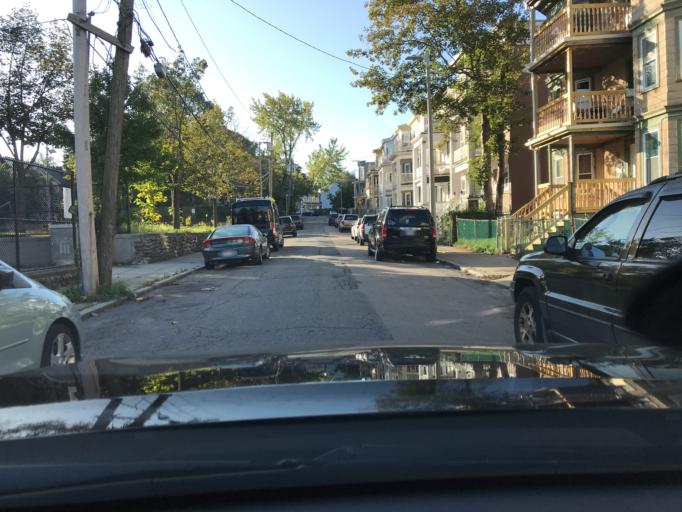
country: US
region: Massachusetts
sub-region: Suffolk County
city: South Boston
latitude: 42.2996
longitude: -71.0764
